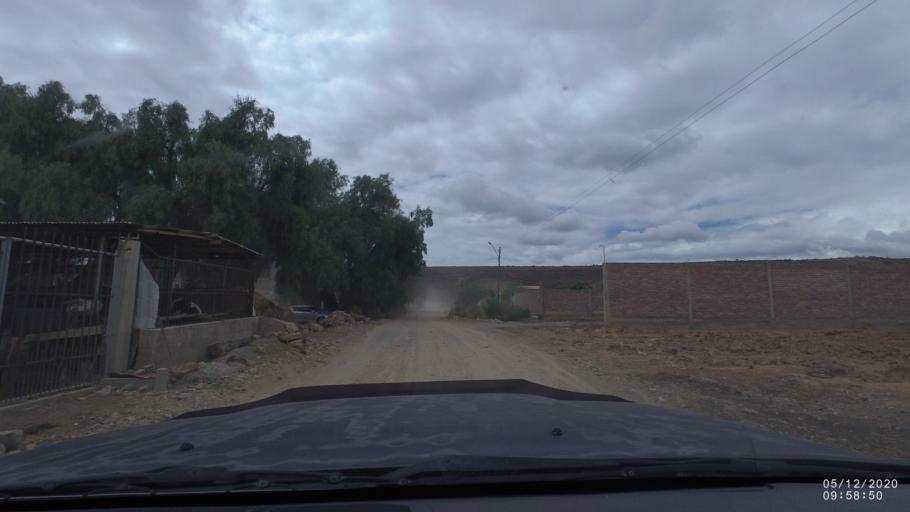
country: BO
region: Cochabamba
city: Sipe Sipe
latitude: -17.4315
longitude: -66.2920
